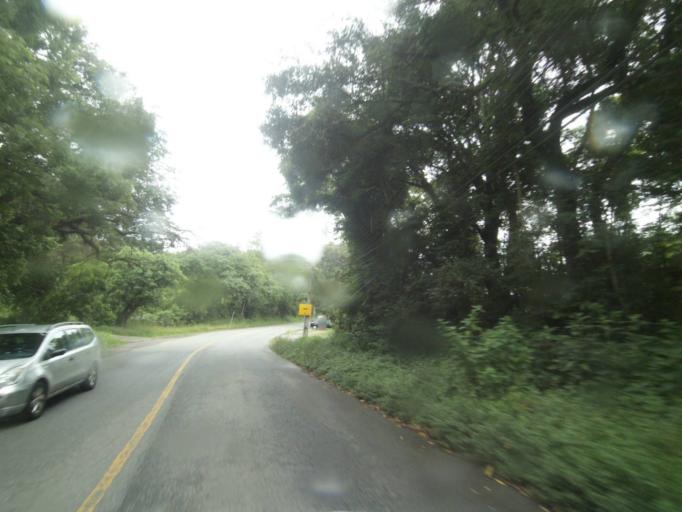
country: BR
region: Parana
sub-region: Curitiba
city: Curitiba
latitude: -25.4270
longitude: -49.3340
